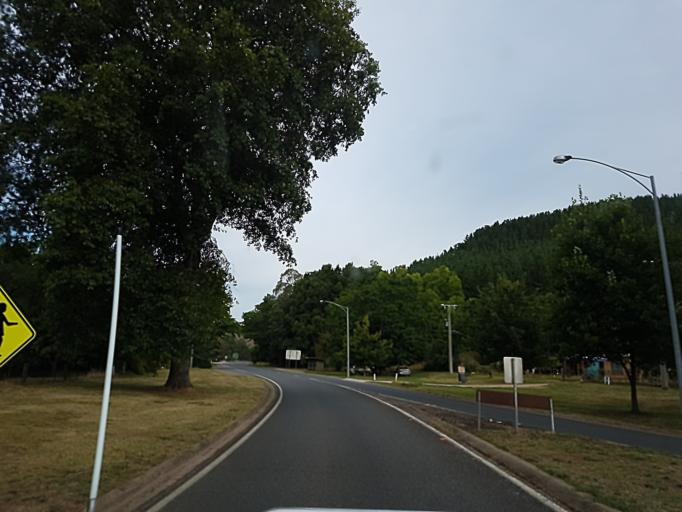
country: AU
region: Victoria
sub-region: Alpine
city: Mount Beauty
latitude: -36.7002
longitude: 146.9092
